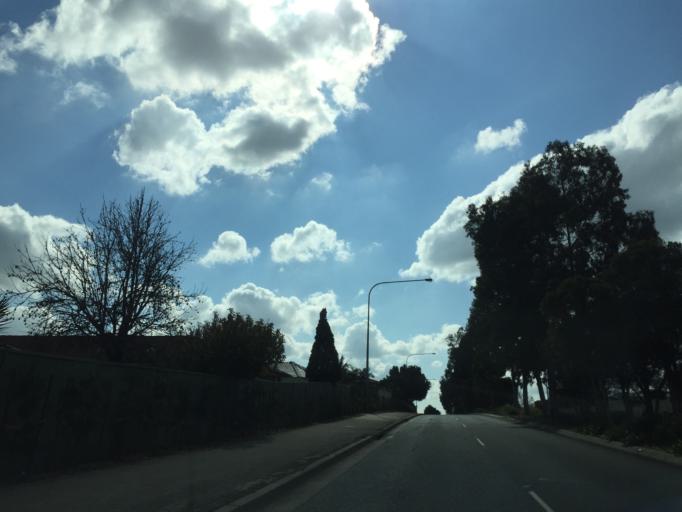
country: AU
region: New South Wales
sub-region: Blacktown
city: Quakers Hill
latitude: -33.7155
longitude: 150.8927
